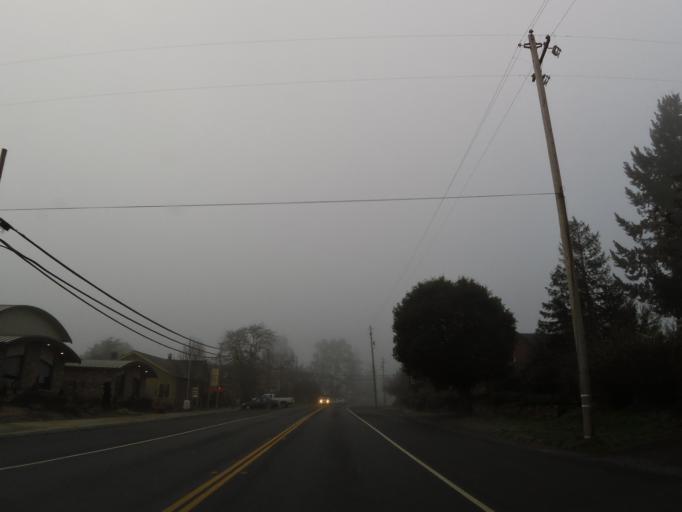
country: US
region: California
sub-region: Mendocino County
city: Boonville
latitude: 39.0099
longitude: -123.3684
